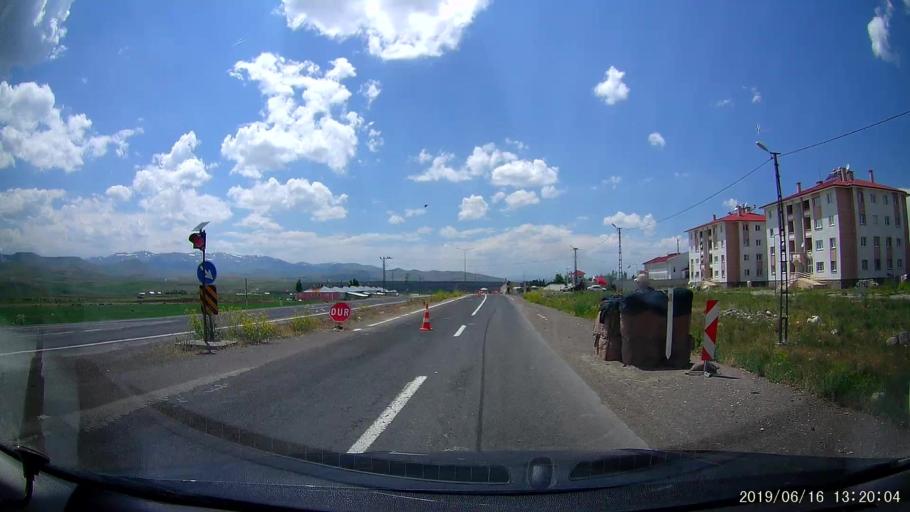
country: TR
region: Agri
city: Taslicay
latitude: 39.6326
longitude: 43.3962
